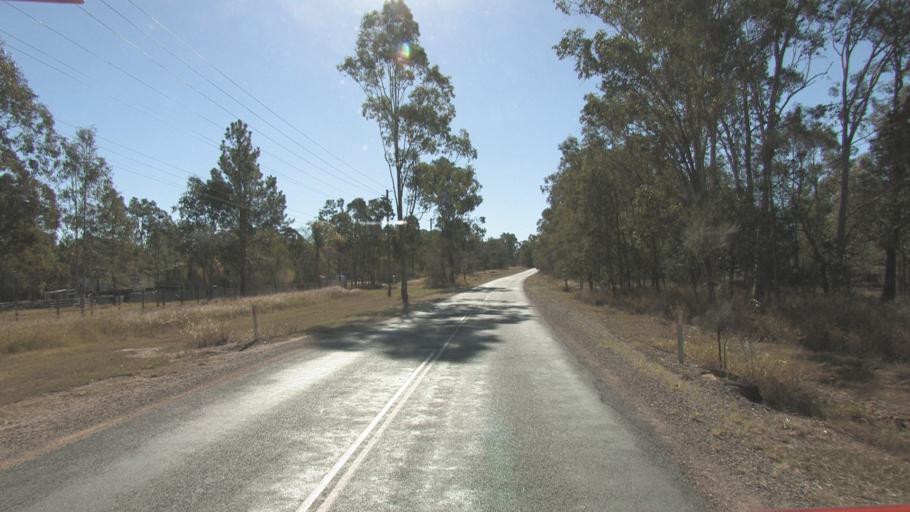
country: AU
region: Queensland
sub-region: Logan
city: North Maclean
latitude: -27.7623
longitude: 152.9967
